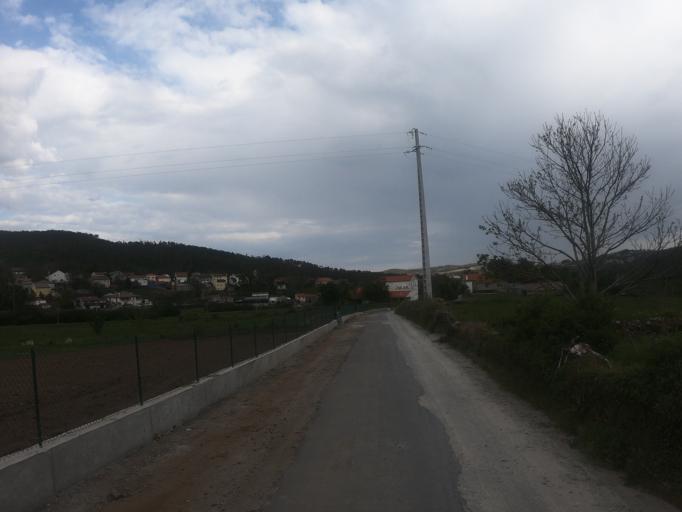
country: PT
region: Vila Real
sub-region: Santa Marta de Penaguiao
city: Santa Marta de Penaguiao
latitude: 41.3021
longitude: -7.8763
